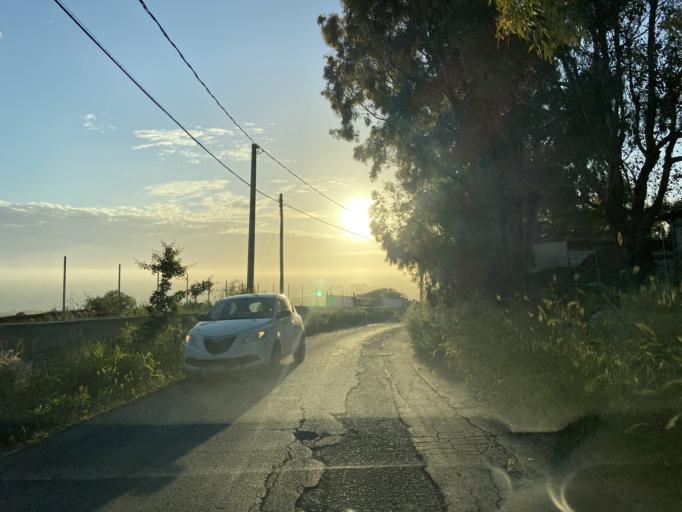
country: IT
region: Latium
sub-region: Citta metropolitana di Roma Capitale
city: Civitavecchia
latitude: 42.0798
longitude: 11.8359
